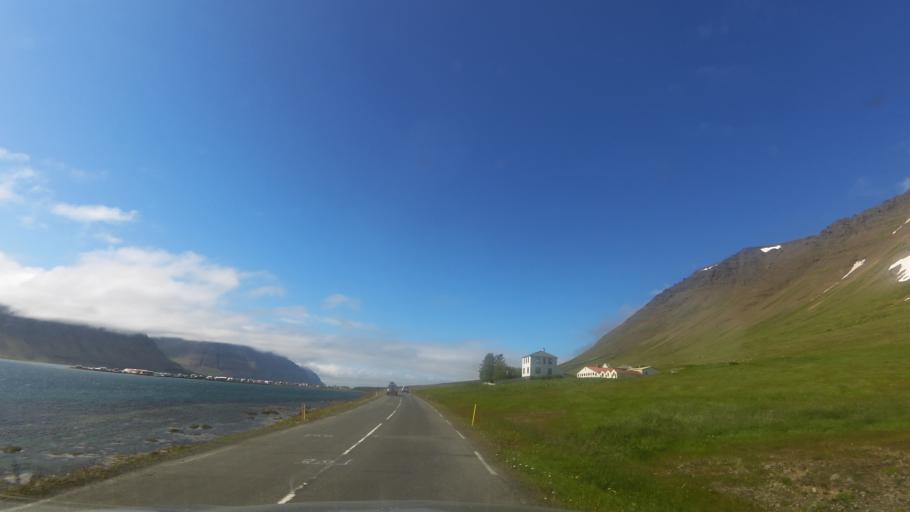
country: IS
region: Westfjords
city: Isafjoerdur
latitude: 66.0484
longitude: -23.4777
